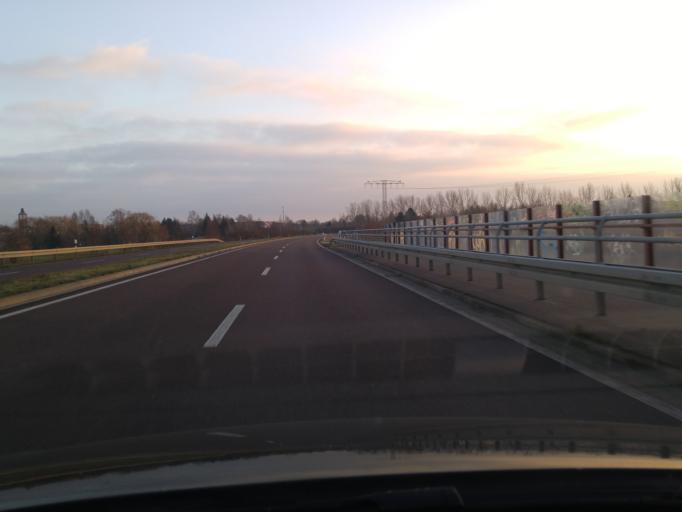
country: DE
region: Saxony
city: Leipzig
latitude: 51.3818
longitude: 12.3420
